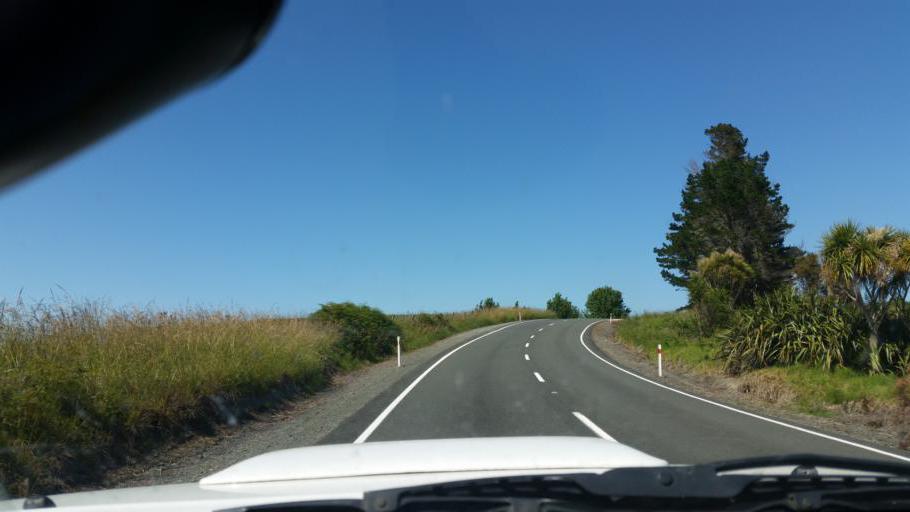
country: NZ
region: Auckland
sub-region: Auckland
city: Wellsford
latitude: -36.2226
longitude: 174.3791
